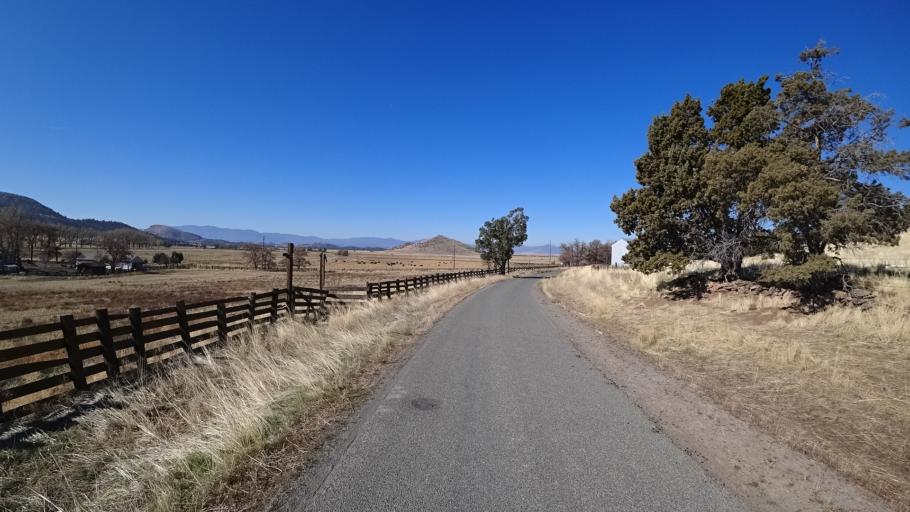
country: US
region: California
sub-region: Siskiyou County
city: Montague
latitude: 41.6878
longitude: -122.3678
